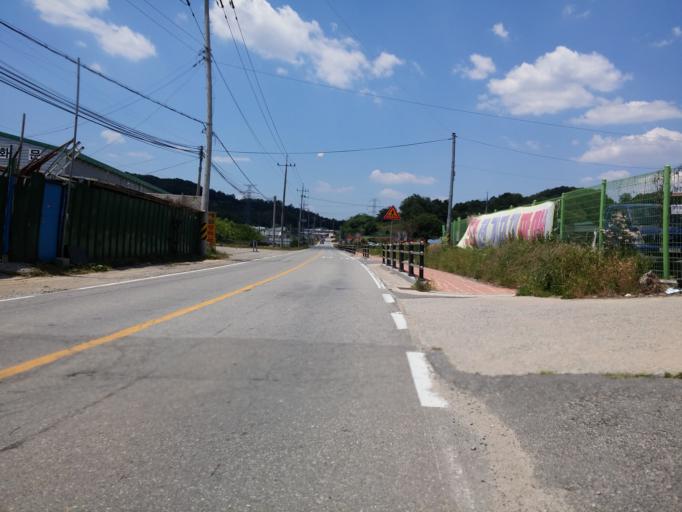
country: KR
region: Chungcheongbuk-do
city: Cheongju-si
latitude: 36.5812
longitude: 127.4474
